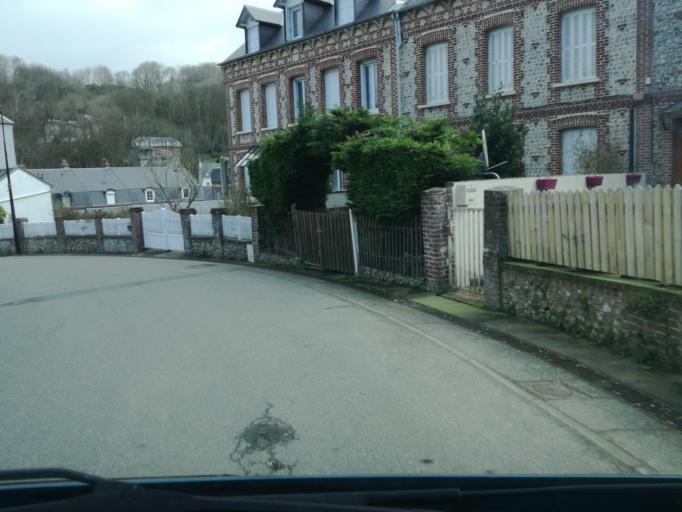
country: FR
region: Haute-Normandie
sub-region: Departement de la Seine-Maritime
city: Yport
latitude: 49.7366
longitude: 0.3152
